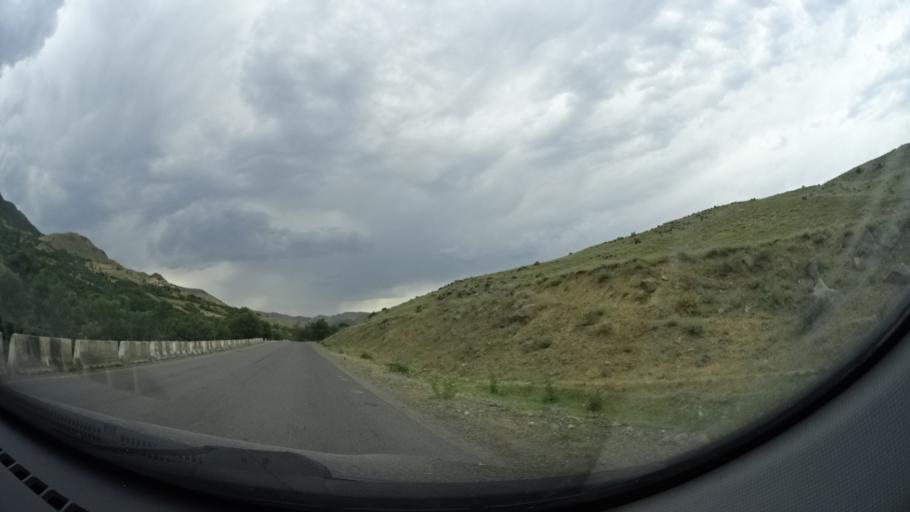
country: GE
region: Samtskhe-Javakheti
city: Aspindza
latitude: 41.5947
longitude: 43.1583
